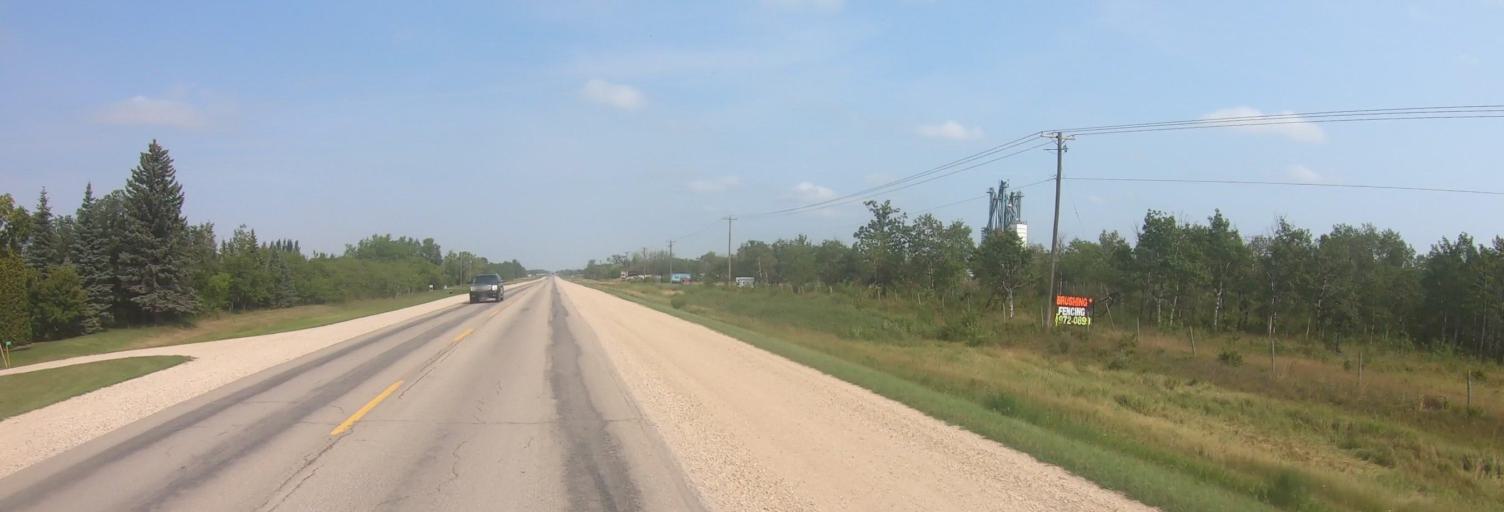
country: CA
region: Manitoba
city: Steinbach
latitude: 49.4925
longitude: -96.6912
